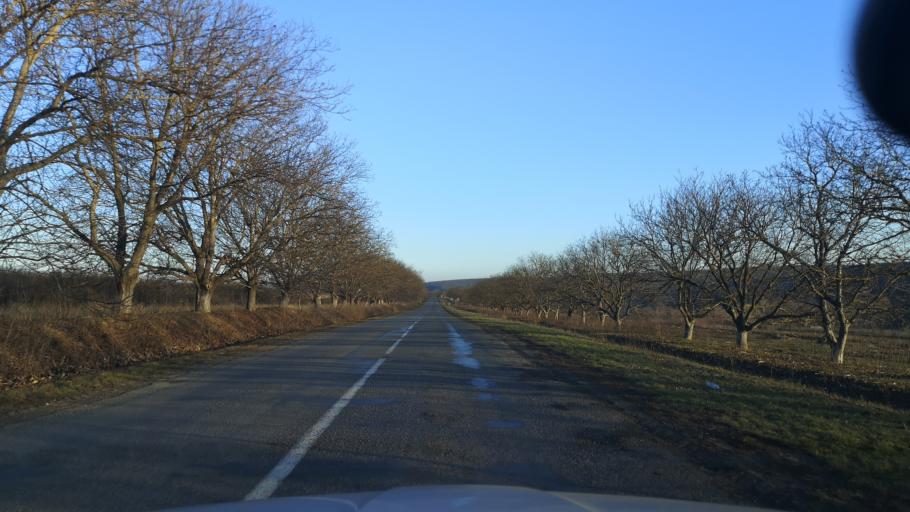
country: MD
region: Orhei
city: Orhei
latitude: 47.2852
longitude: 28.8274
